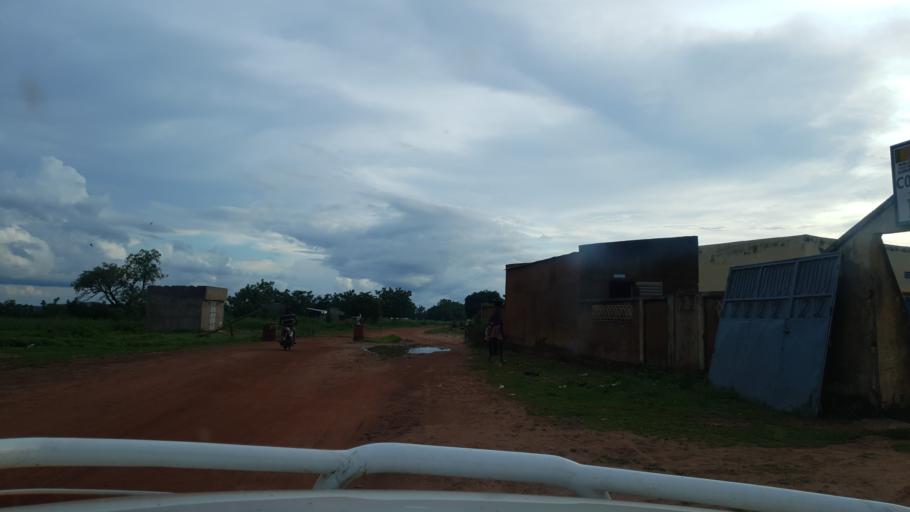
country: CI
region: Savanes
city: Tengrela
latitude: 10.5445
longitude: -6.9170
